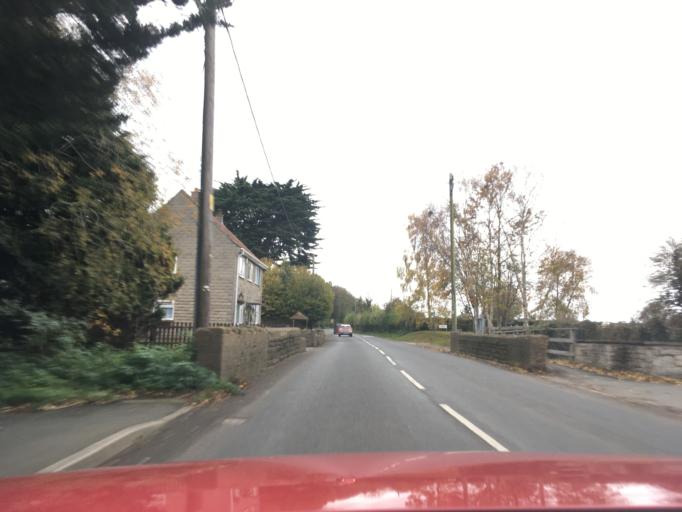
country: GB
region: England
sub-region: Somerset
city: Yeovil
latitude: 50.9993
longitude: -2.5839
